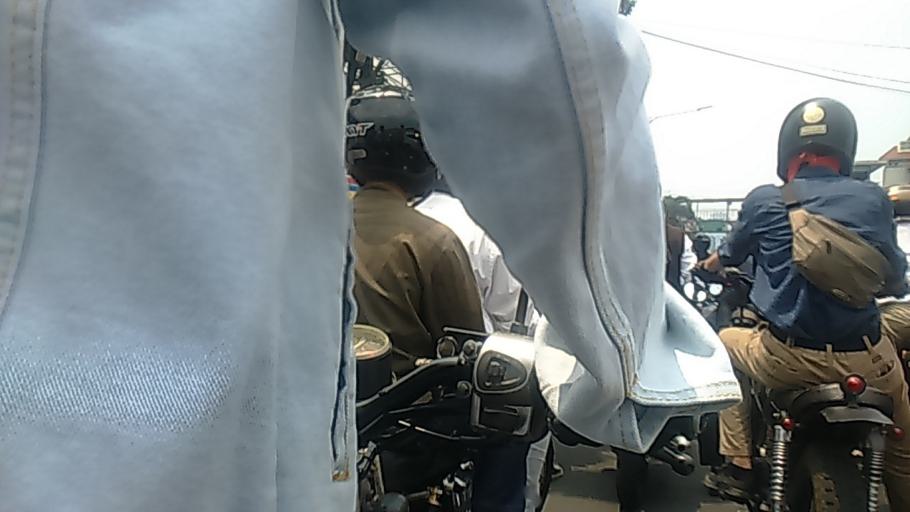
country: ID
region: Jakarta Raya
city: Jakarta
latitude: -6.2574
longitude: 106.8281
